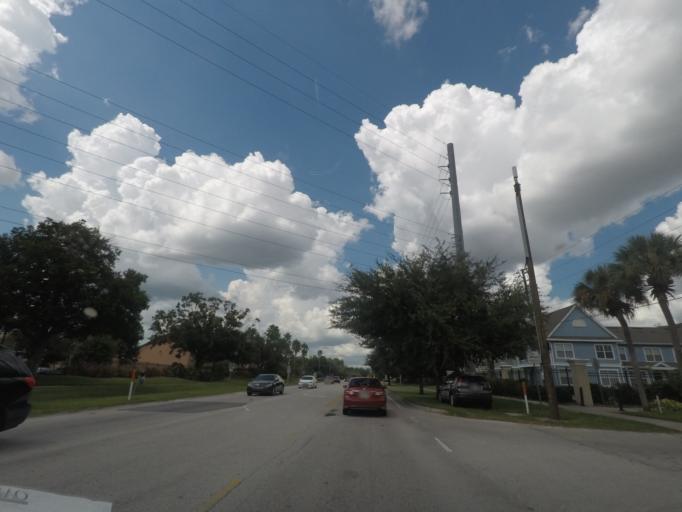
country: US
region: Florida
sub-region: Osceola County
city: Kissimmee
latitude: 28.3120
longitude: -81.4450
